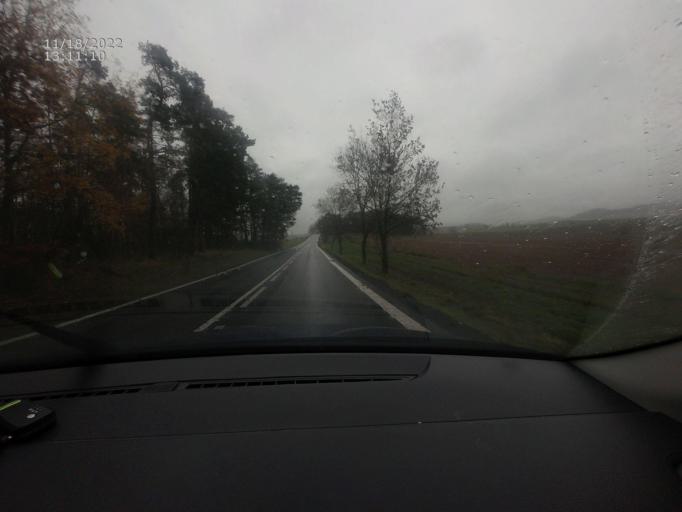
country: CZ
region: Plzensky
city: Hradek
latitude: 49.3289
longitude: 13.5790
